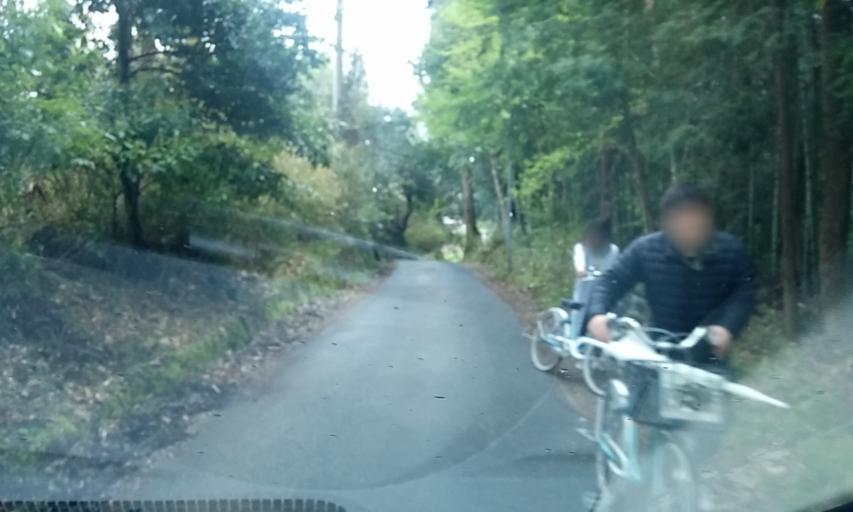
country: JP
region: Kyoto
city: Miyazu
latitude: 35.5856
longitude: 135.1986
